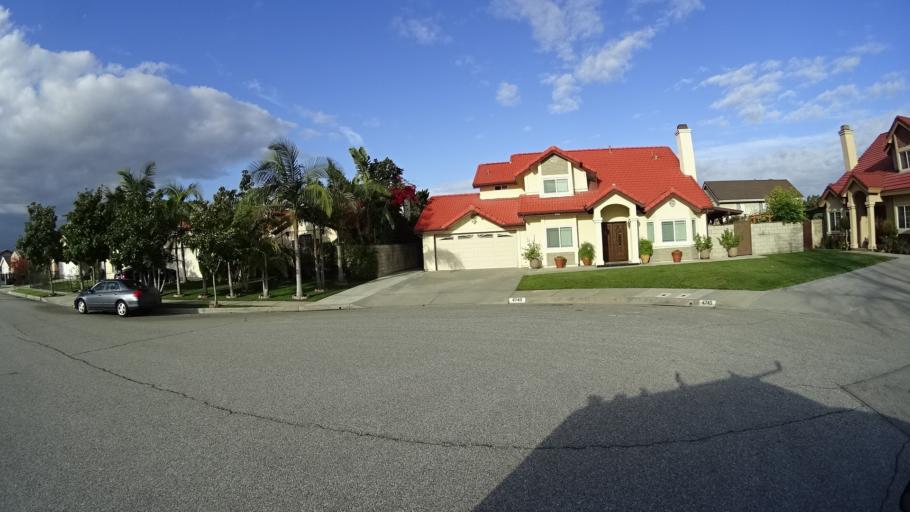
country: US
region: California
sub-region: Los Angeles County
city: Baldwin Park
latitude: 34.0986
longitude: -117.9725
